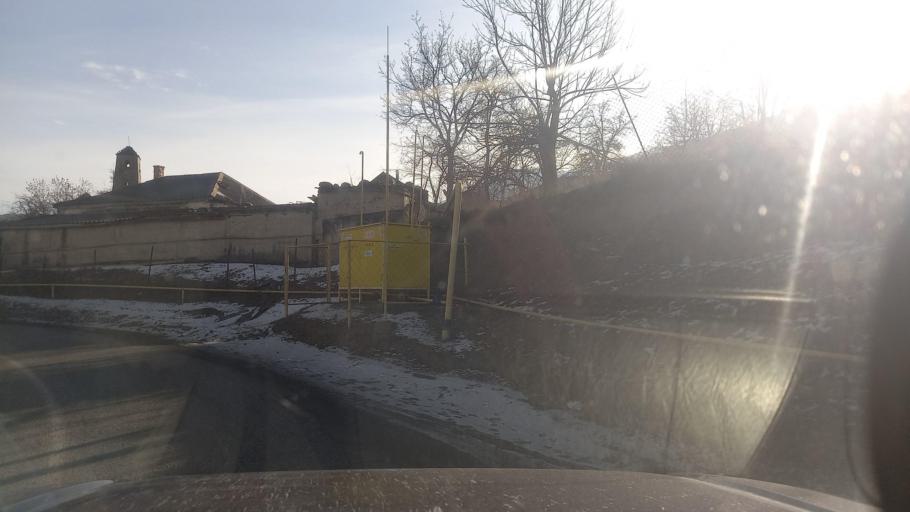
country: RU
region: Ingushetiya
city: Dzhayrakh
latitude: 42.8262
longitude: 44.6718
